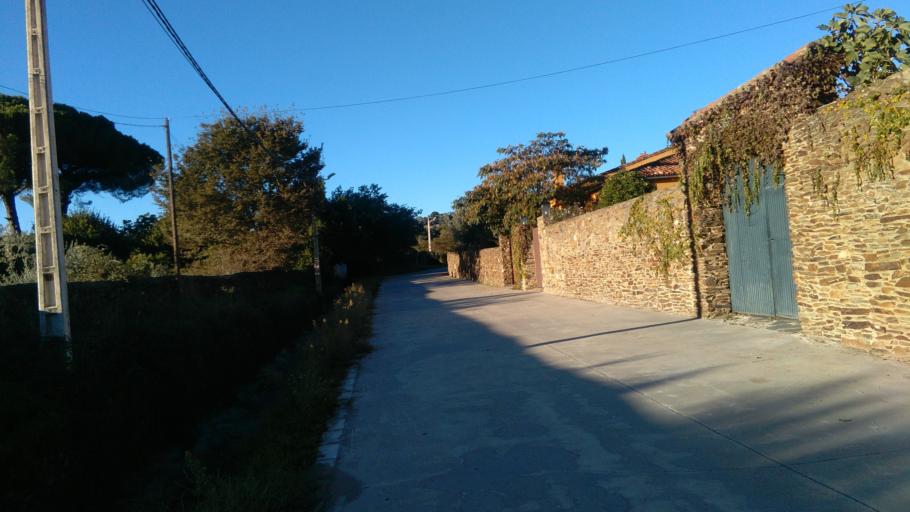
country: ES
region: Extremadura
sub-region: Provincia de Caceres
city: Herguijuela
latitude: 39.3953
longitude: -5.7821
